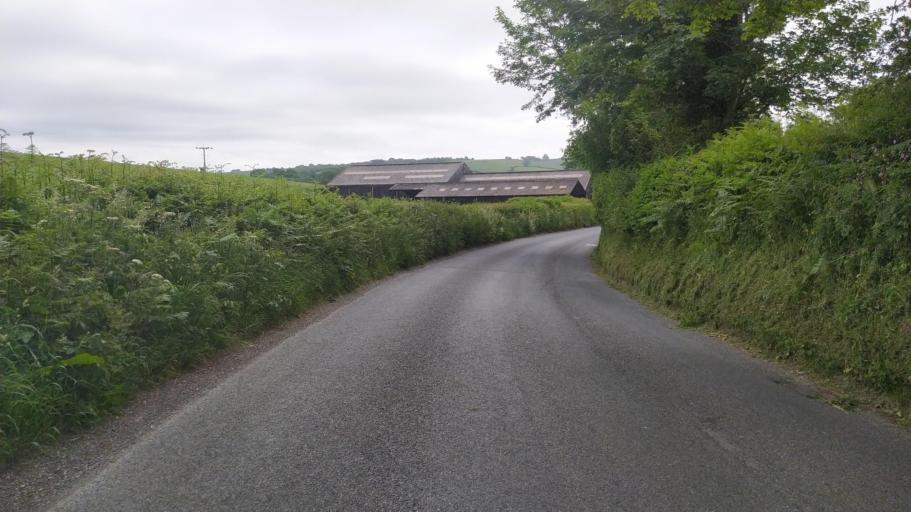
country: GB
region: England
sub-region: Somerset
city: Yeovil
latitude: 50.8385
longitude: -2.5853
